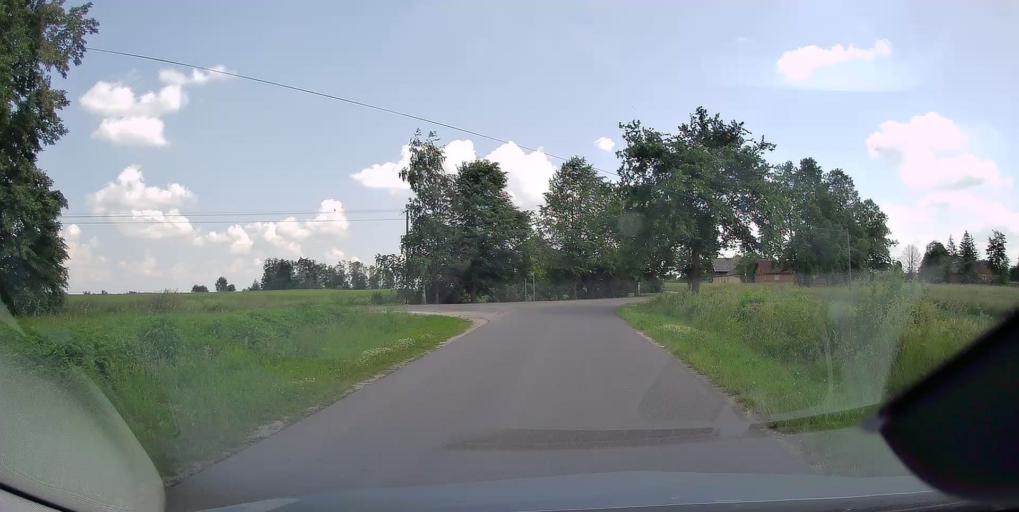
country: PL
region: Lodz Voivodeship
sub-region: Powiat tomaszowski
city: Czerniewice
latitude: 51.6920
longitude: 20.2162
